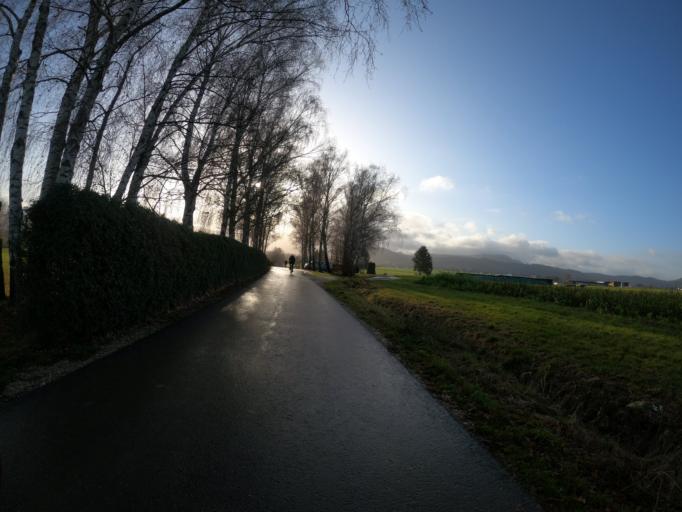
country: DE
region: Baden-Wuerttemberg
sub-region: Regierungsbezirk Stuttgart
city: Boll
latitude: 48.6539
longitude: 9.6201
